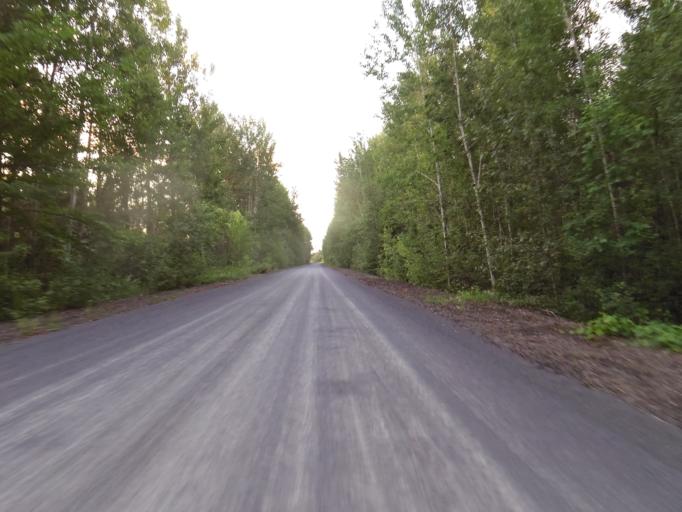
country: CA
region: Ontario
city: Arnprior
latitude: 45.3916
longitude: -76.3222
